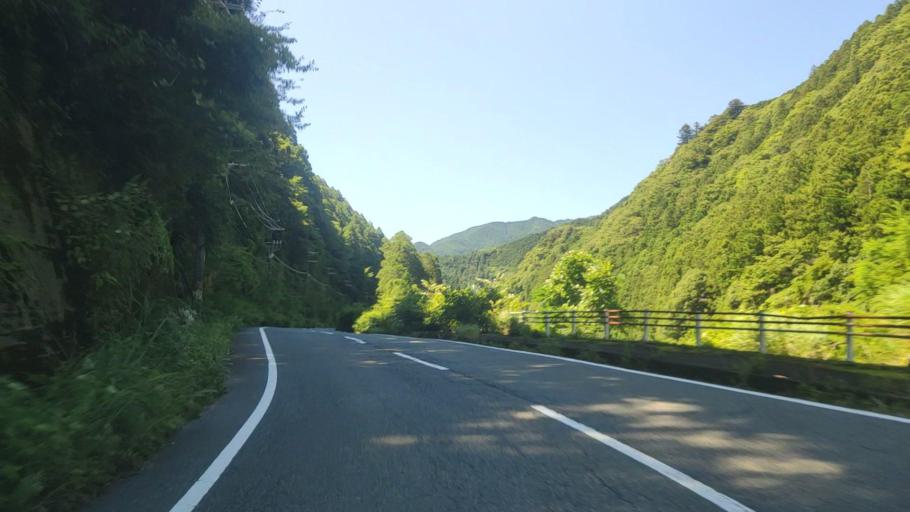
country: JP
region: Nara
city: Yoshino-cho
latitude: 34.2961
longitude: 136.0019
